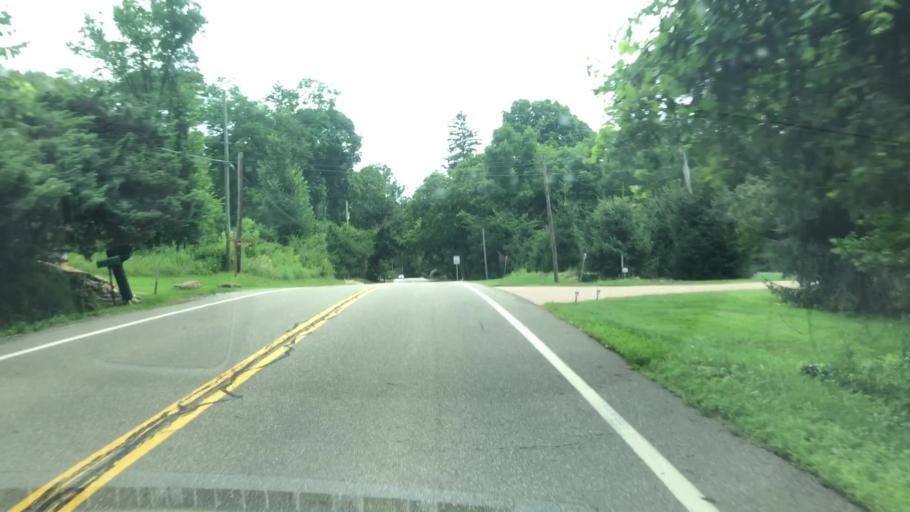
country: US
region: Ohio
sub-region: Summit County
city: Montrose-Ghent
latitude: 41.1570
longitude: -81.6229
